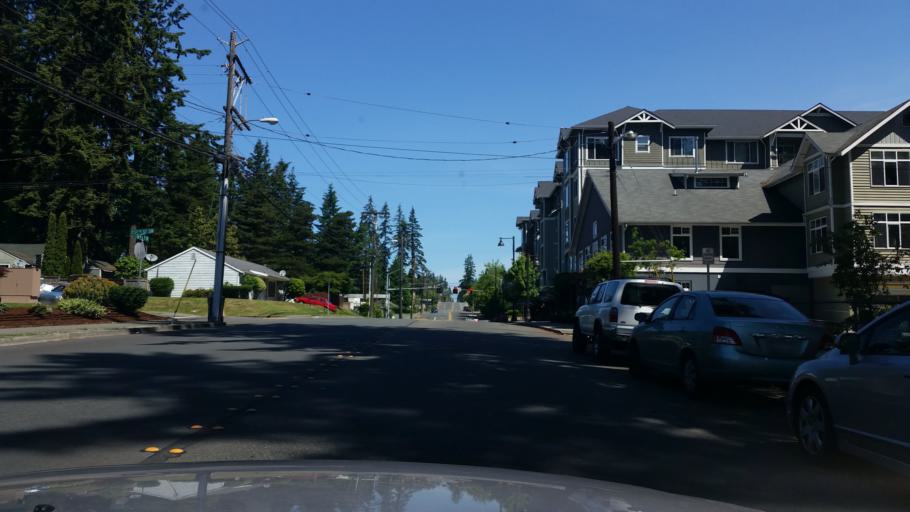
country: US
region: Washington
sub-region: Snohomish County
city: Mountlake Terrace
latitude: 47.7835
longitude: -122.3084
